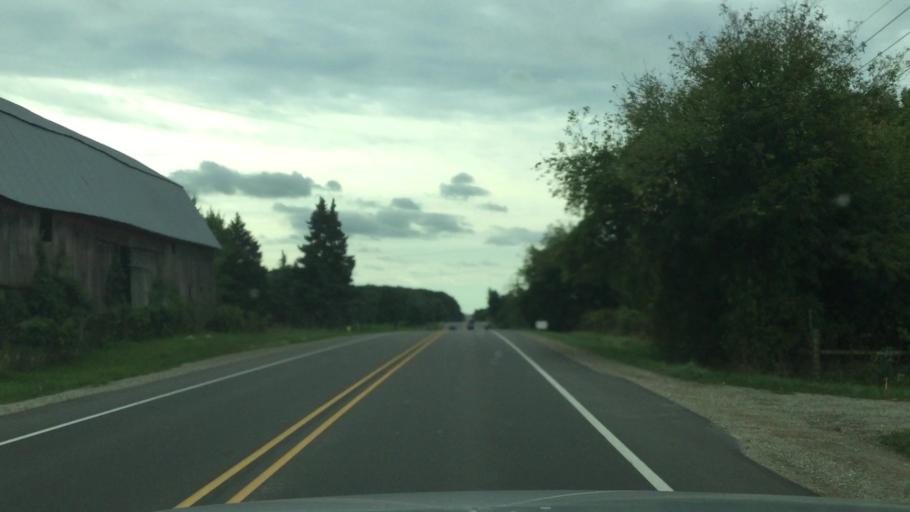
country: US
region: Michigan
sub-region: Livingston County
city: Howell
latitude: 42.6142
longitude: -83.8750
